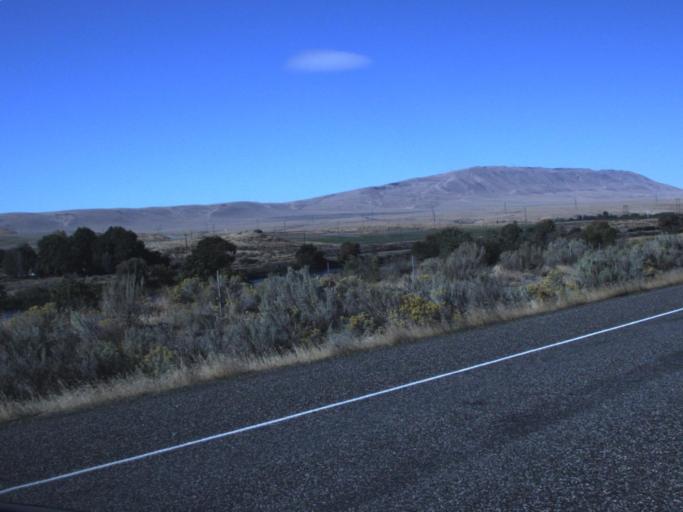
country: US
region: Washington
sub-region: Benton County
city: West Richland
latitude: 46.3707
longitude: -119.3997
